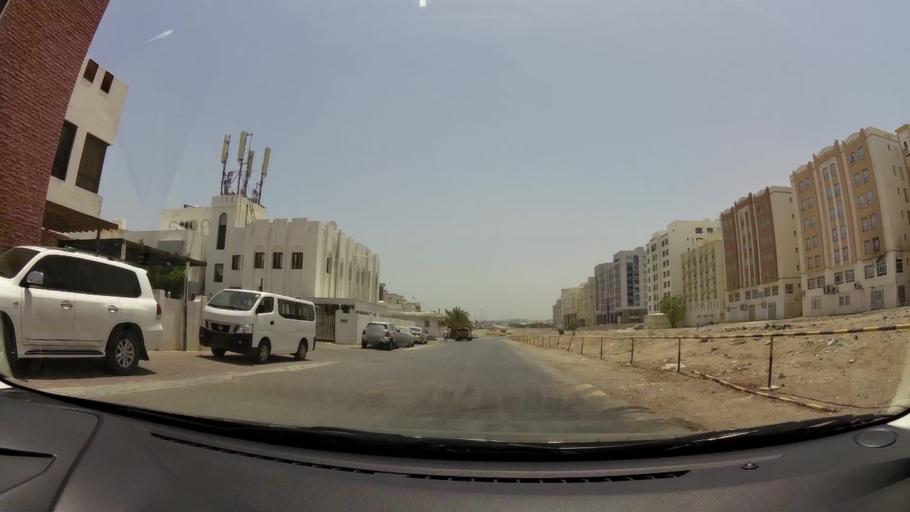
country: OM
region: Muhafazat Masqat
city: Bawshar
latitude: 23.5842
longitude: 58.4241
